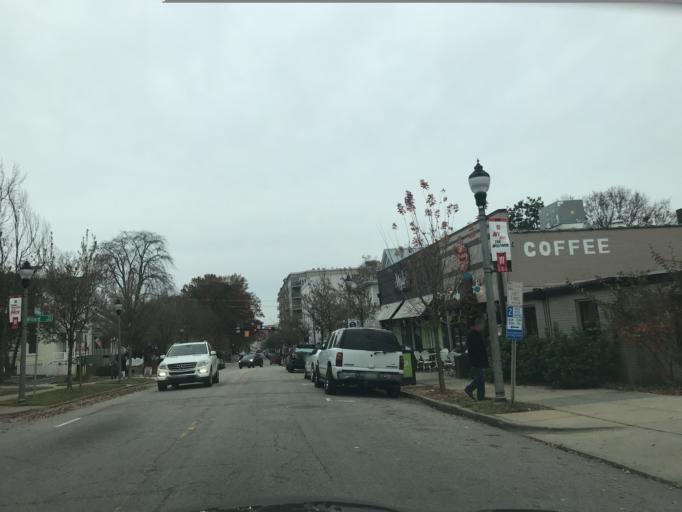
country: US
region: North Carolina
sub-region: Wake County
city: Raleigh
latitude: 35.7818
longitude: -78.6475
